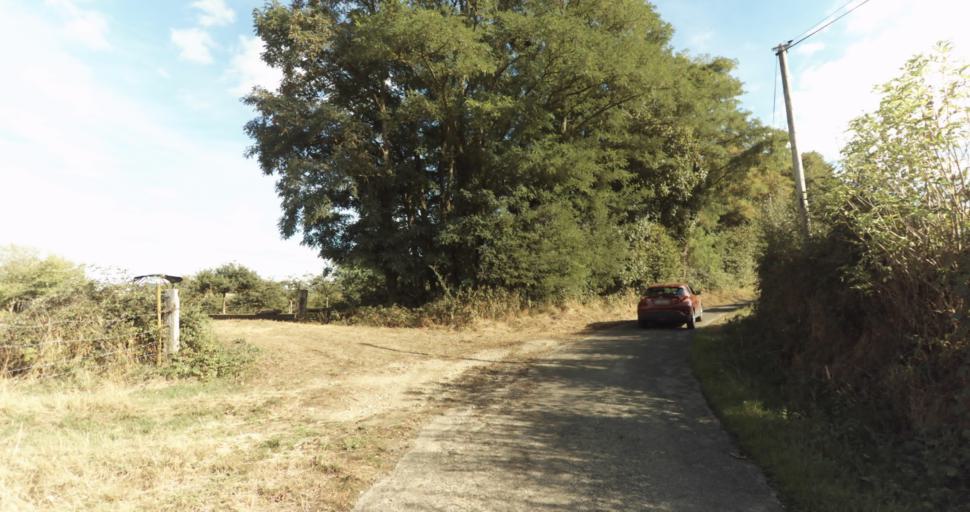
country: FR
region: Lower Normandy
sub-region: Departement de l'Orne
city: Vimoutiers
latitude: 48.9257
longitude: 0.1234
